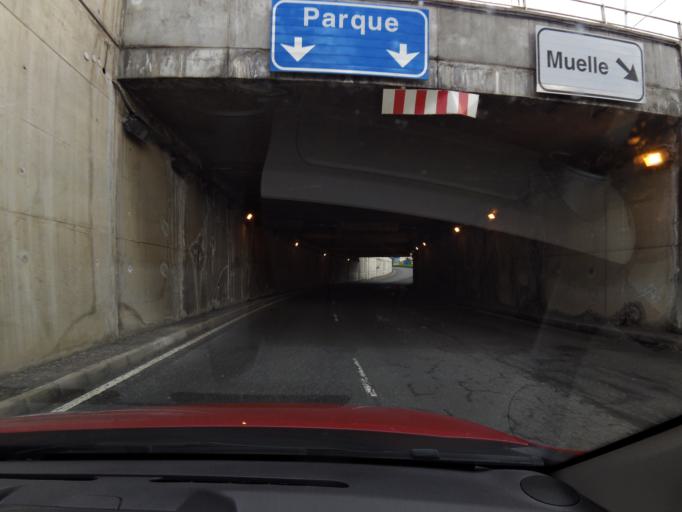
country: ES
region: Canary Islands
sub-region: Provincia de Las Palmas
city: Las Palmas de Gran Canaria
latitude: 28.1396
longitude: -15.4291
